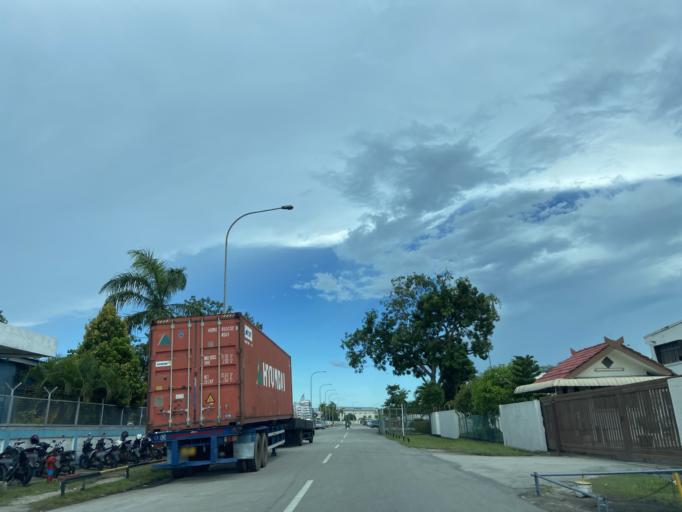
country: SG
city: Singapore
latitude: 1.0628
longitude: 104.0296
